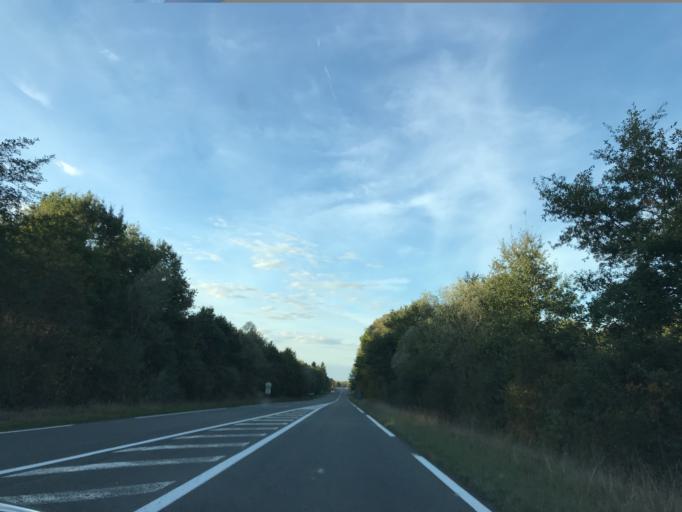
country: FR
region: Auvergne
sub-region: Departement de l'Allier
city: Saint-Yorre
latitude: 46.0124
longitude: 3.4861
